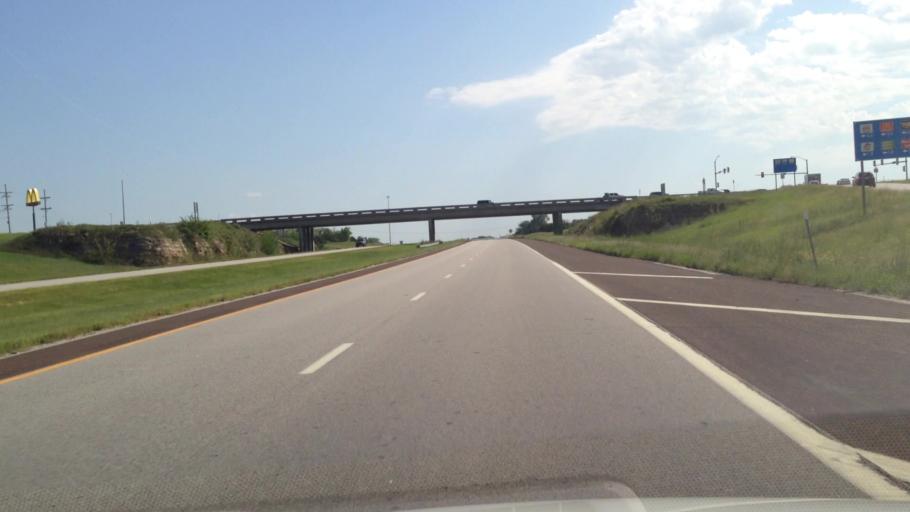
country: US
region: Kansas
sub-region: Miami County
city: Louisburg
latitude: 38.6228
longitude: -94.6952
